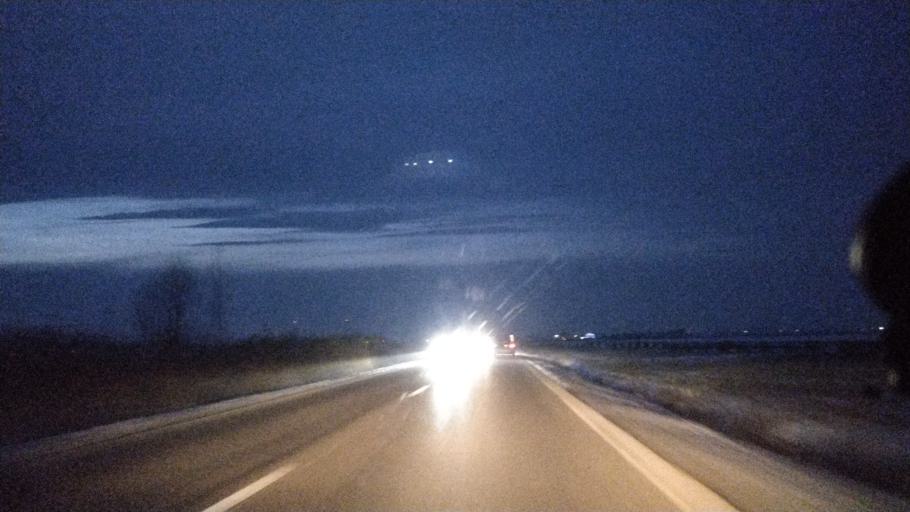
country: RO
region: Vrancea
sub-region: Comuna Milcovul
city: Milcovul
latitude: 45.6728
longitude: 27.2568
